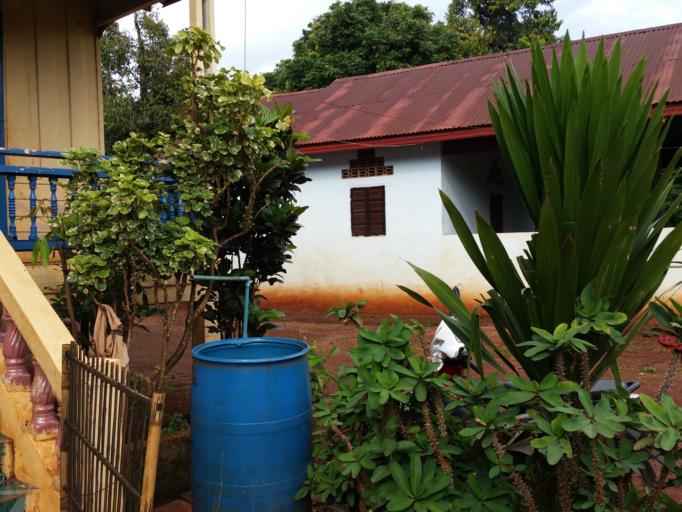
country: LA
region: Champasak
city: Pakxe
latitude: 15.2131
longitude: 105.9473
